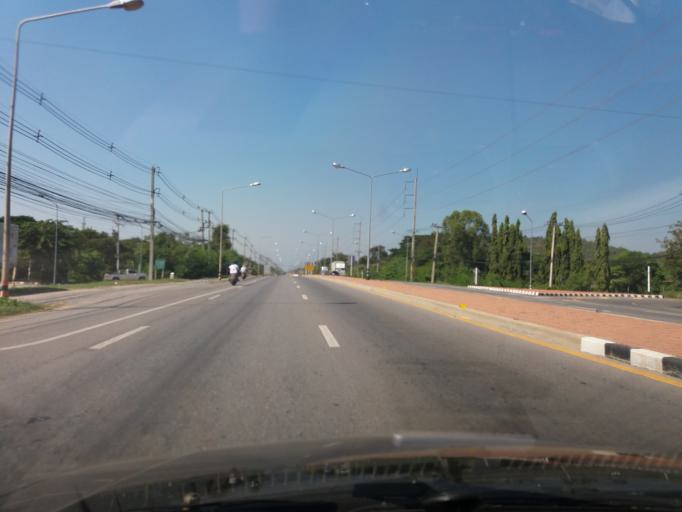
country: TH
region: Chai Nat
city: Chai Nat
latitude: 15.1973
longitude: 100.1253
